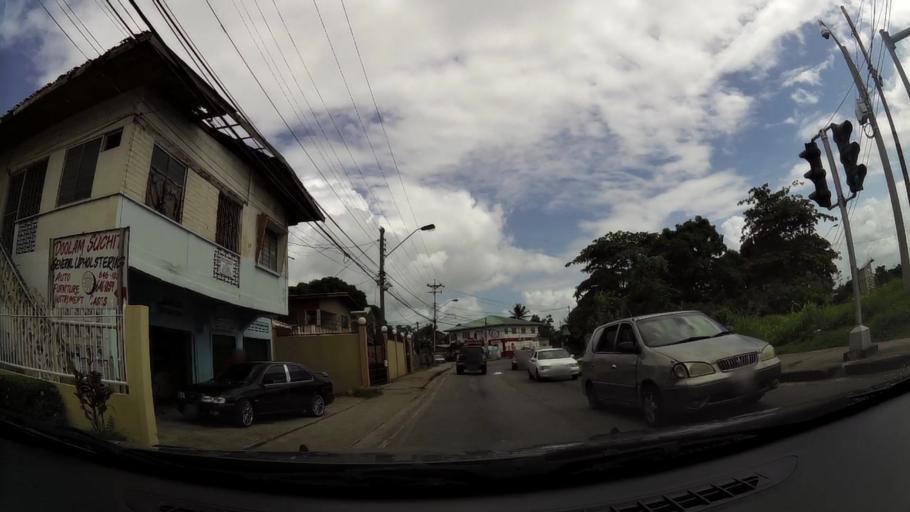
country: TT
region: Tunapuna/Piarco
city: Arouca
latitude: 10.6343
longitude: -61.3285
